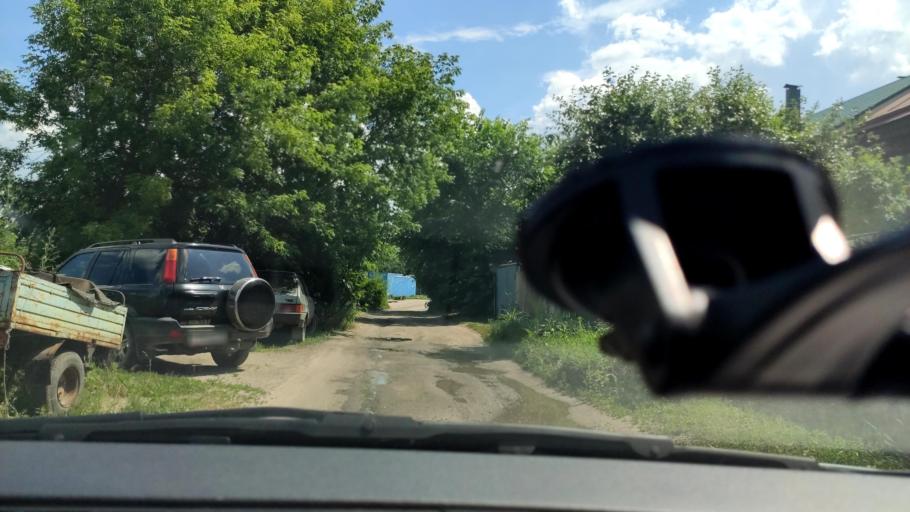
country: RU
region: Voronezj
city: Ramon'
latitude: 51.8941
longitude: 39.3423
